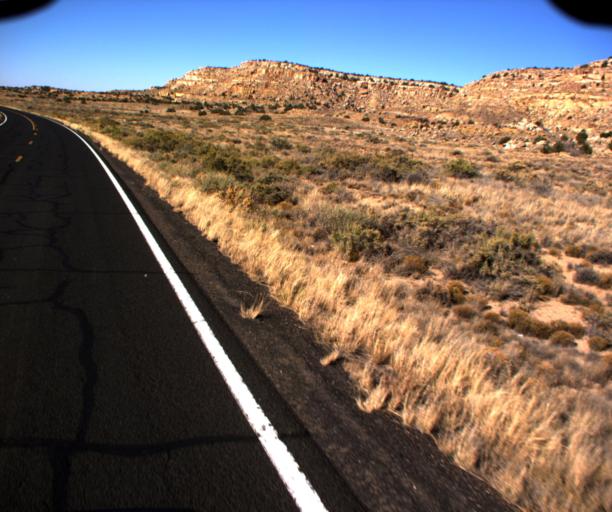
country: US
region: Arizona
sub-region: Navajo County
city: First Mesa
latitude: 35.8404
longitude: -110.2547
